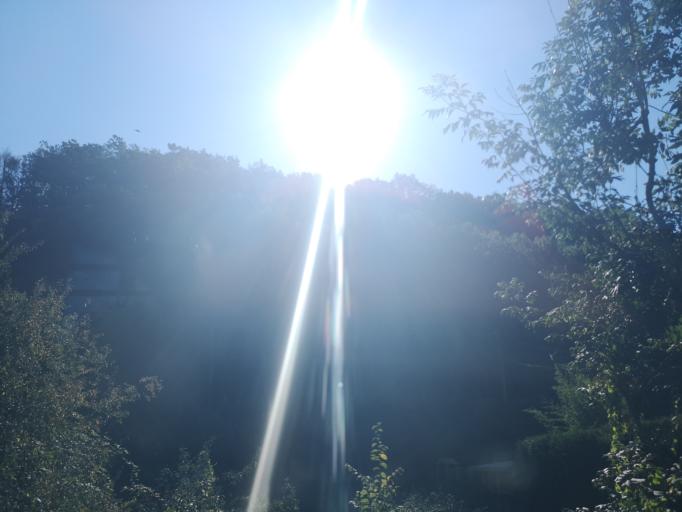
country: DE
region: North Rhine-Westphalia
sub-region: Regierungsbezirk Koln
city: Kreuzau
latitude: 50.7263
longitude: 6.4596
